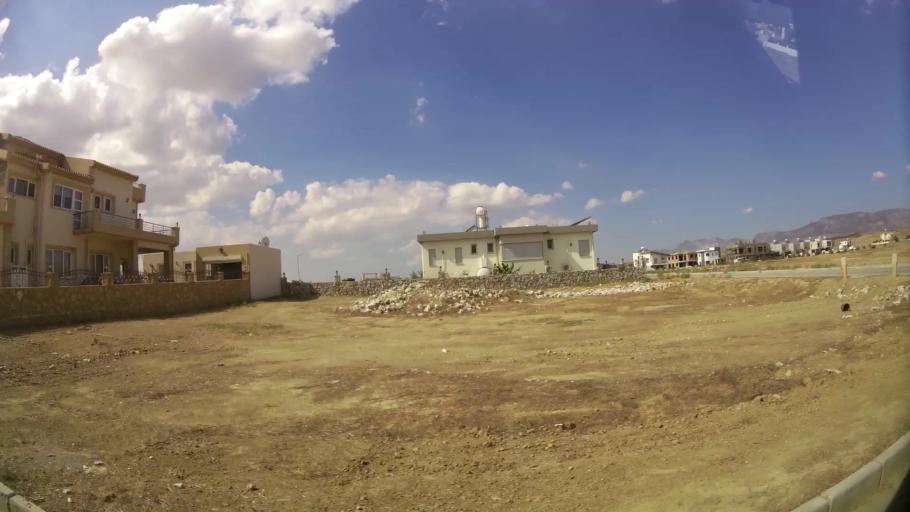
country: CY
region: Lefkosia
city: Nicosia
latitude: 35.2215
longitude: 33.2915
